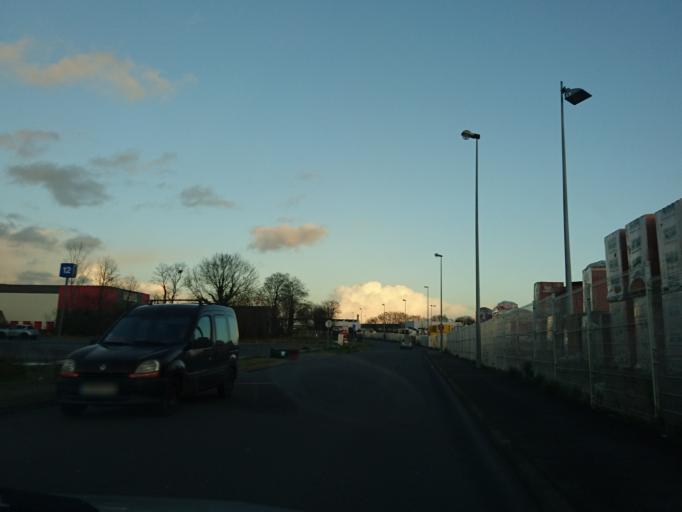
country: FR
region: Brittany
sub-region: Departement du Finistere
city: Gouesnou
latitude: 48.4316
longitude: -4.4480
